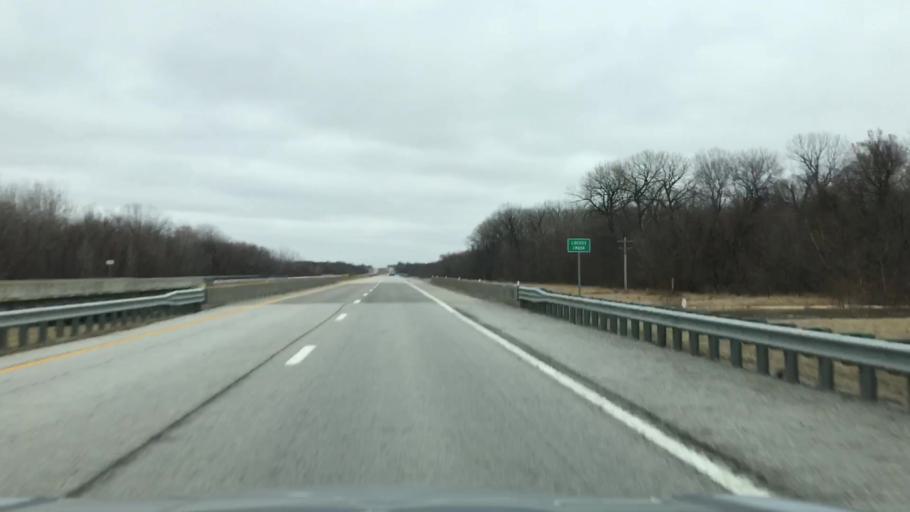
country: US
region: Missouri
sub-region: Linn County
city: Linneus
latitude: 39.7779
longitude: -93.2277
